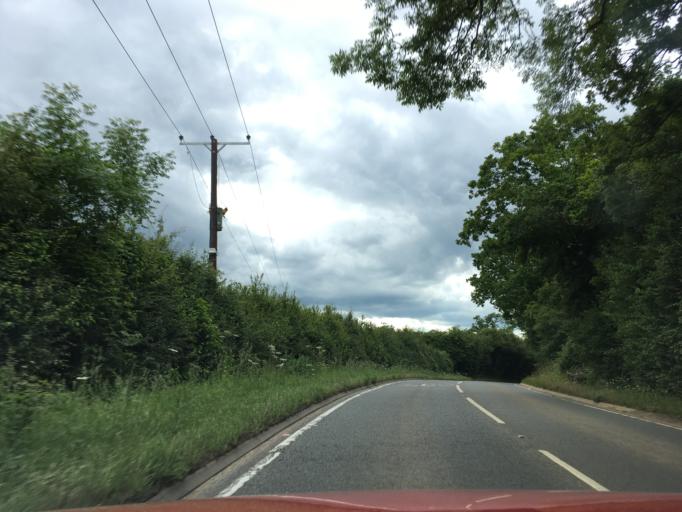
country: GB
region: England
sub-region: Central Bedfordshire
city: Potsgrove
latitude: 51.9549
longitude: -0.6457
